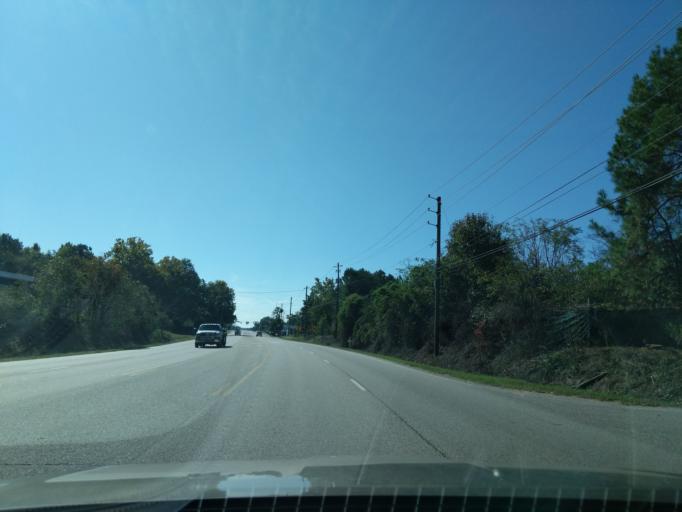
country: US
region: Georgia
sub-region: Richmond County
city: Augusta
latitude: 33.4198
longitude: -82.0072
